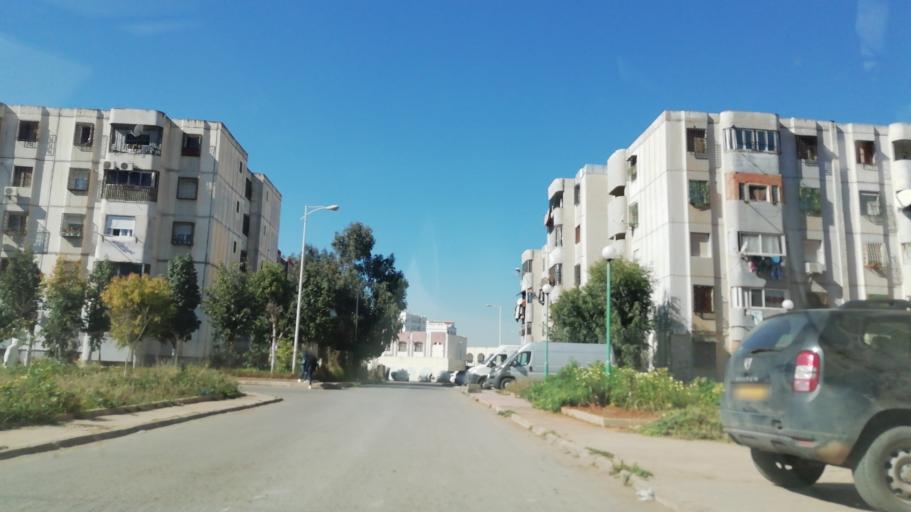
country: DZ
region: Oran
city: Oran
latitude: 35.6866
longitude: -0.6115
